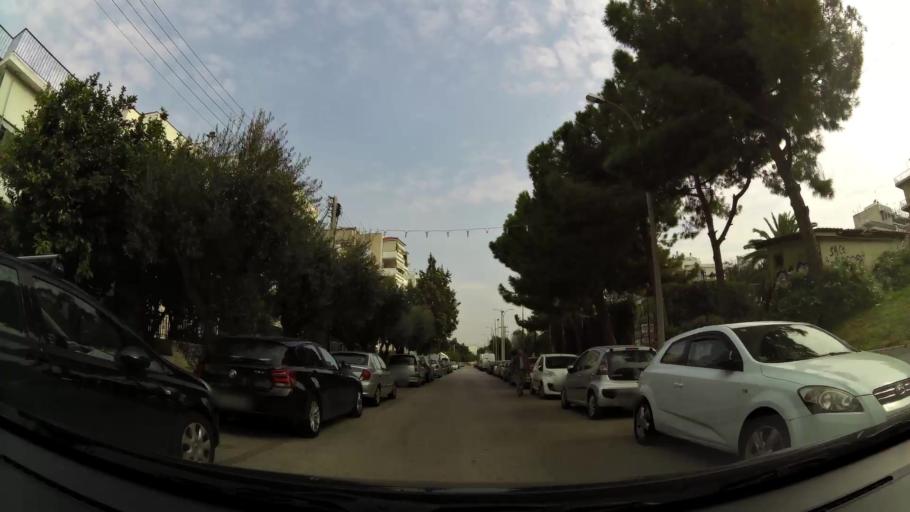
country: GR
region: Attica
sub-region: Nomarchia Athinas
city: Kallithea
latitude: 37.9606
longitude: 23.6992
